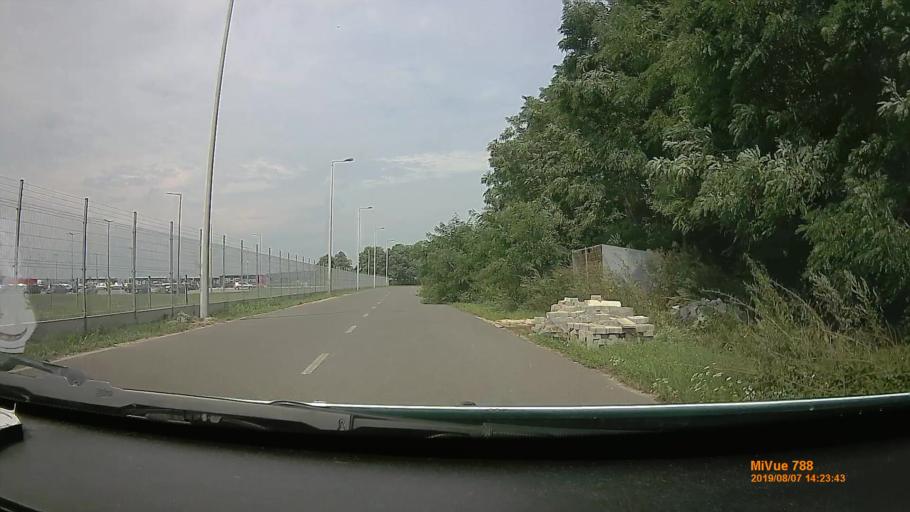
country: HU
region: Borsod-Abauj-Zemplen
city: Szikszo
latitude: 48.1741
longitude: 20.9243
